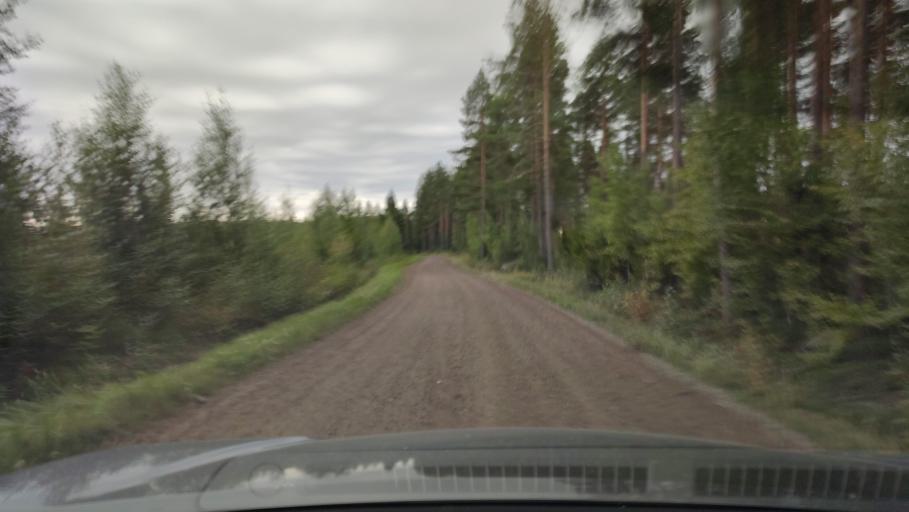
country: FI
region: Southern Ostrobothnia
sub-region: Suupohja
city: Karijoki
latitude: 62.2220
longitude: 21.5717
